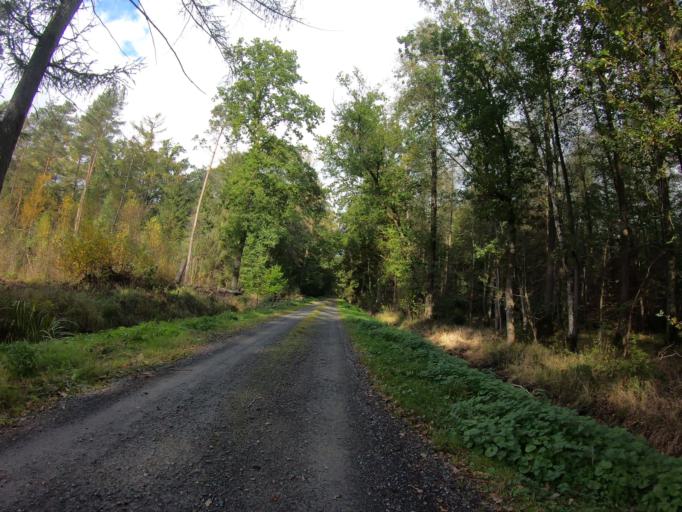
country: DE
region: Lower Saxony
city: Wahrenholz
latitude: 52.5913
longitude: 10.6296
